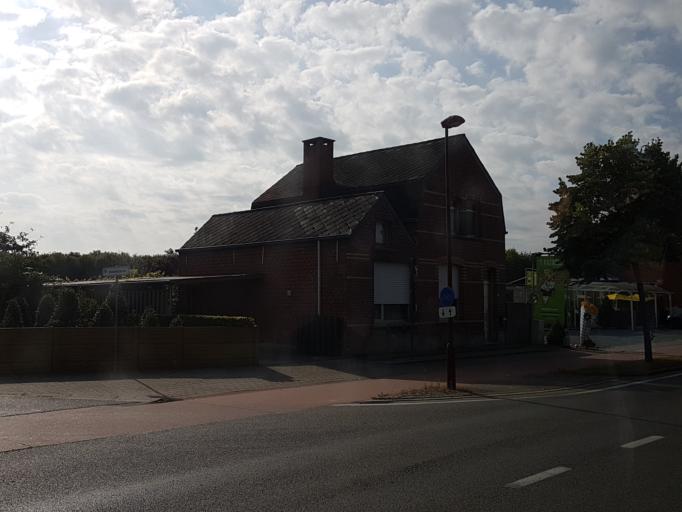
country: BE
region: Flanders
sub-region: Provincie Antwerpen
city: Olen
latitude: 51.1279
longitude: 4.8671
